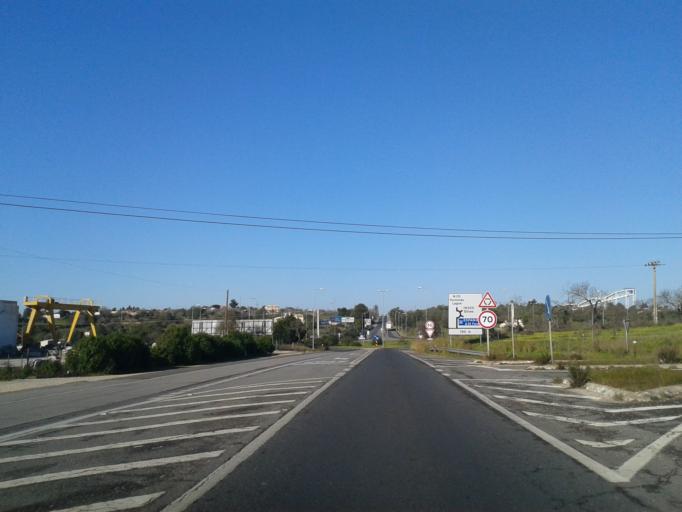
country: PT
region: Faro
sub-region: Silves
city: Armacao de Pera
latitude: 37.1329
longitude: -8.3565
